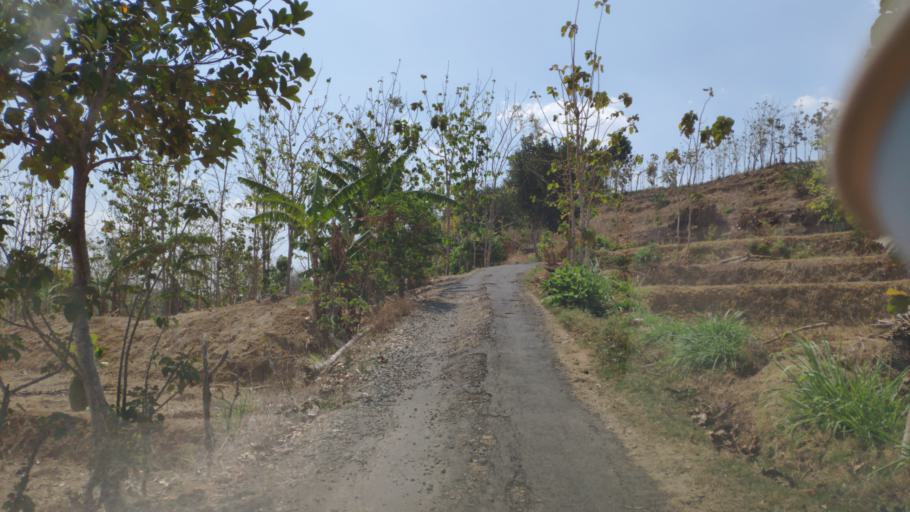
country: ID
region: Central Java
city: Guyangan
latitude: -6.9413
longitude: 111.1441
